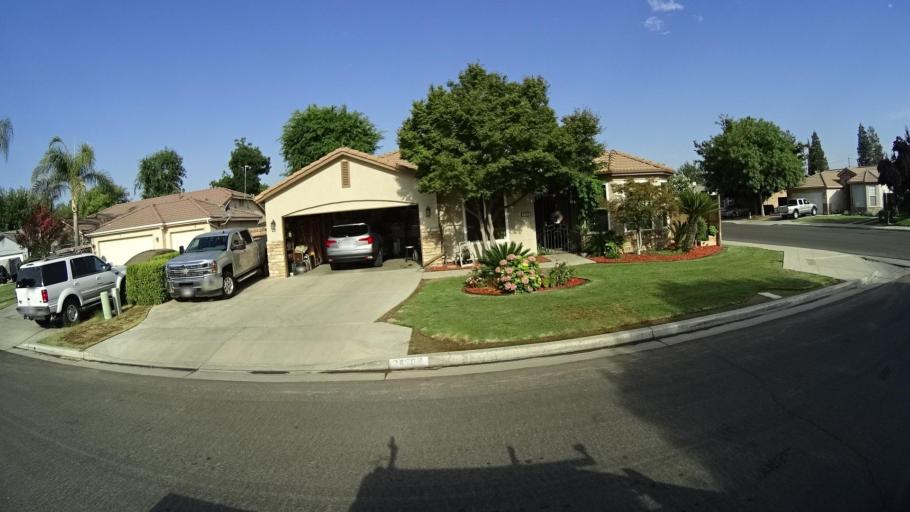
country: US
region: California
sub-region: Fresno County
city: Sunnyside
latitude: 36.7127
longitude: -119.6947
